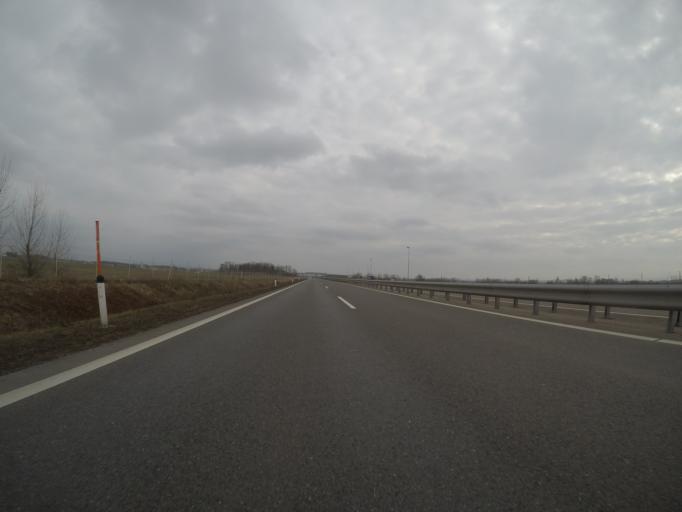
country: SI
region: Turnisce
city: Turnisce
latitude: 46.6222
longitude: 16.2976
